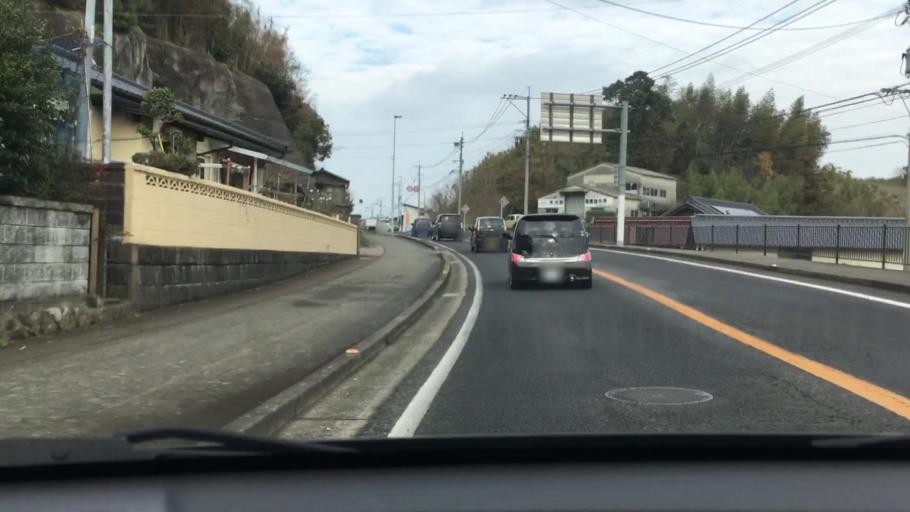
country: JP
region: Saga Prefecture
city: Imaricho-ko
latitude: 33.3089
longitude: 129.9275
